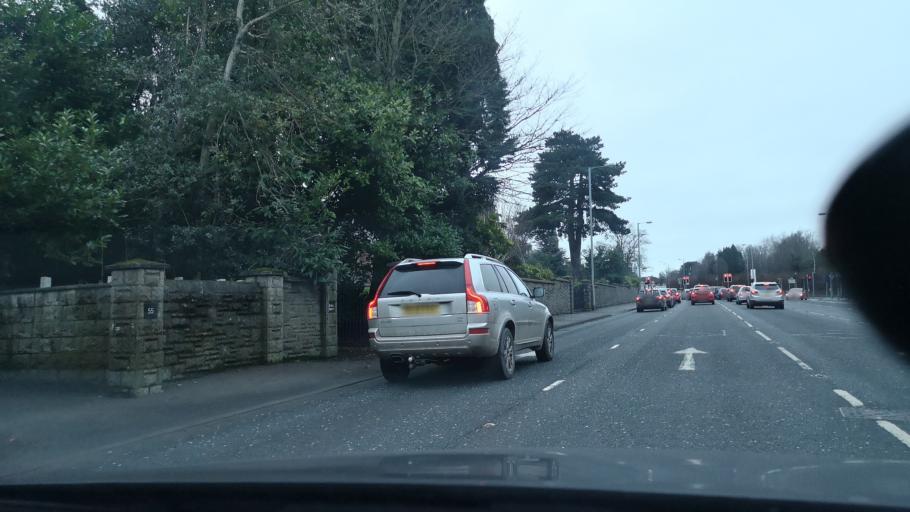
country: GB
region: Northern Ireland
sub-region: Castlereagh District
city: Castlereagh
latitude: 54.5910
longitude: -5.8557
